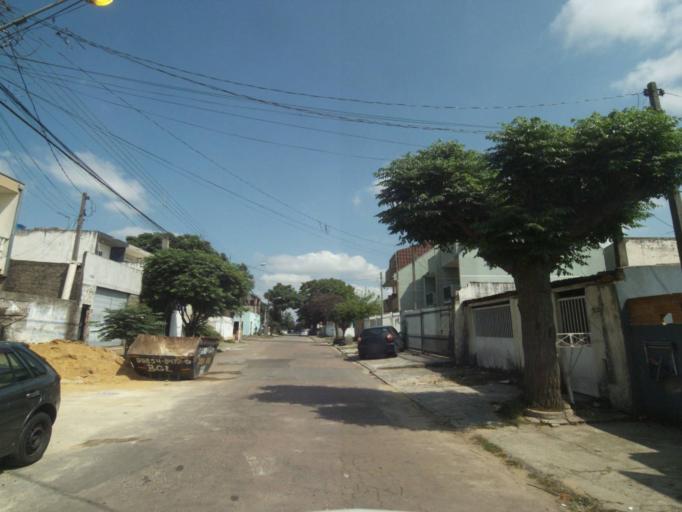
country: BR
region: Parana
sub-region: Sao Jose Dos Pinhais
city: Sao Jose dos Pinhais
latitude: -25.5426
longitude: -49.2644
